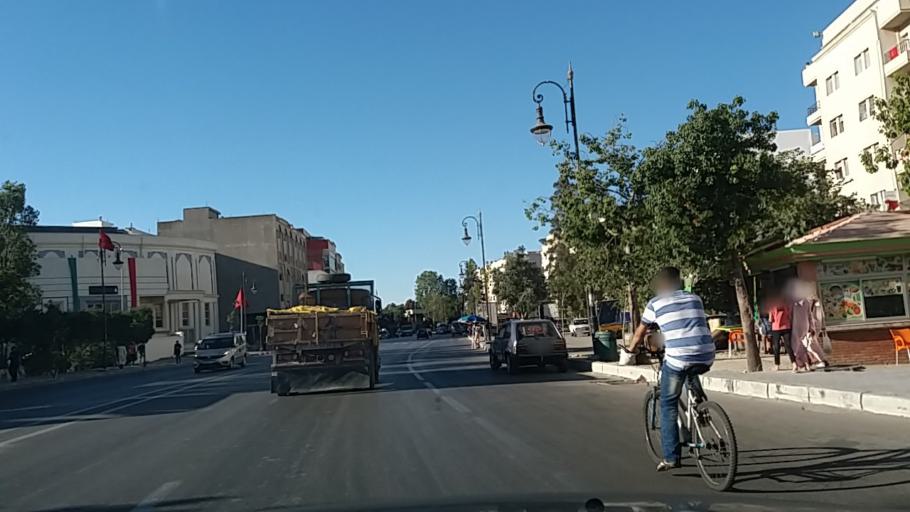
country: MA
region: Tanger-Tetouan
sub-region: Tanger-Assilah
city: Tangier
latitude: 35.7446
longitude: -5.7990
